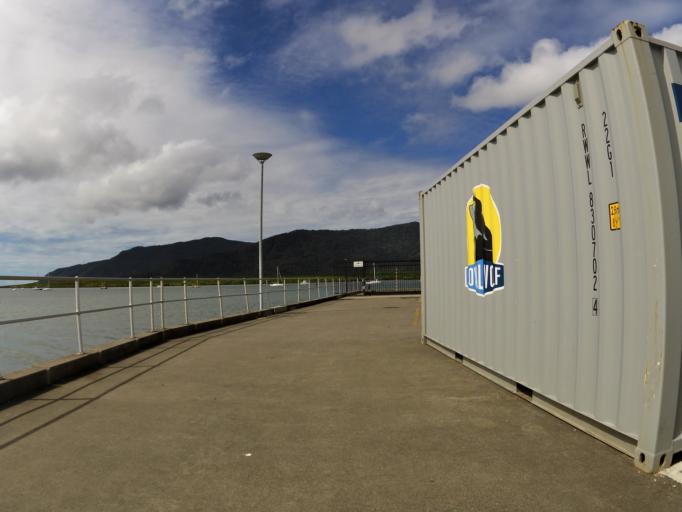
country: AU
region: Queensland
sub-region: Cairns
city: Cairns
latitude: -16.9171
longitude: 145.7830
